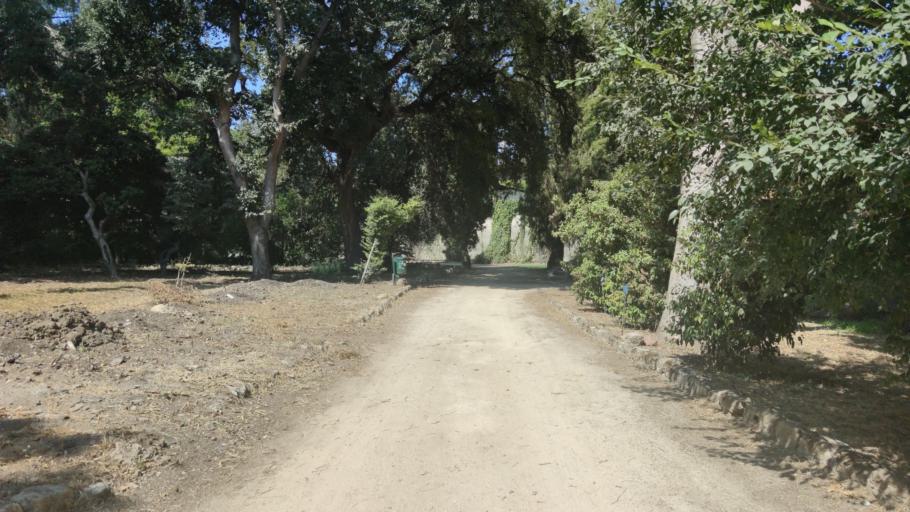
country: IT
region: Sicily
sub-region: Palermo
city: Palermo
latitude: 38.1098
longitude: 13.3751
